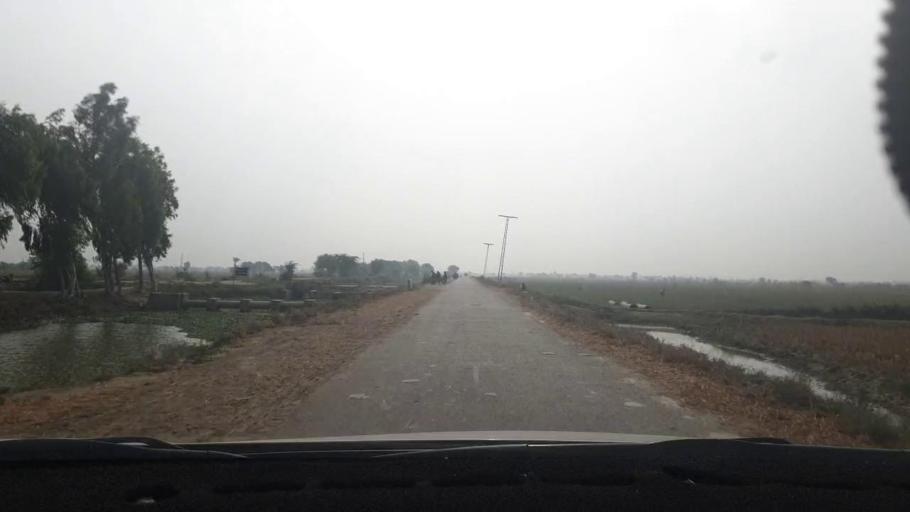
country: PK
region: Sindh
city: Tando Muhammad Khan
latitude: 25.0786
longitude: 68.5323
